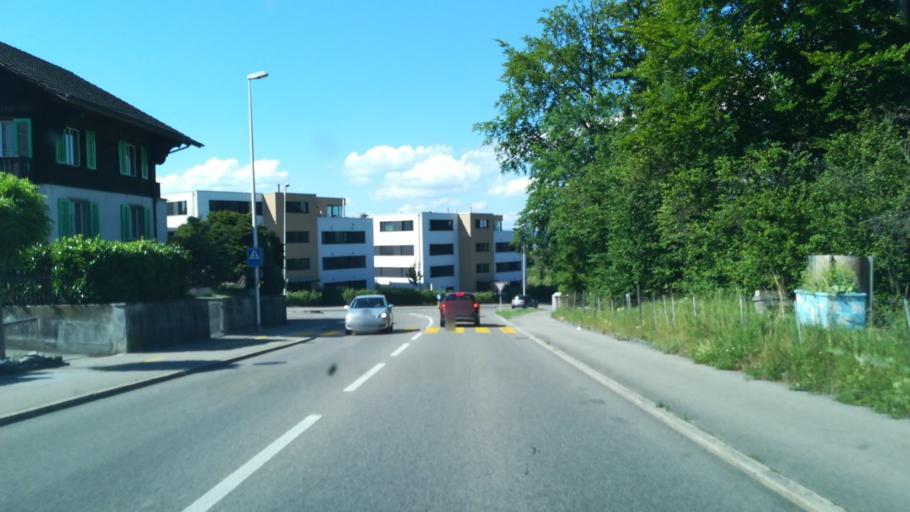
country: CH
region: Thurgau
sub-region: Kreuzlingen District
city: Kreuzlingen
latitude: 47.6400
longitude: 9.1663
